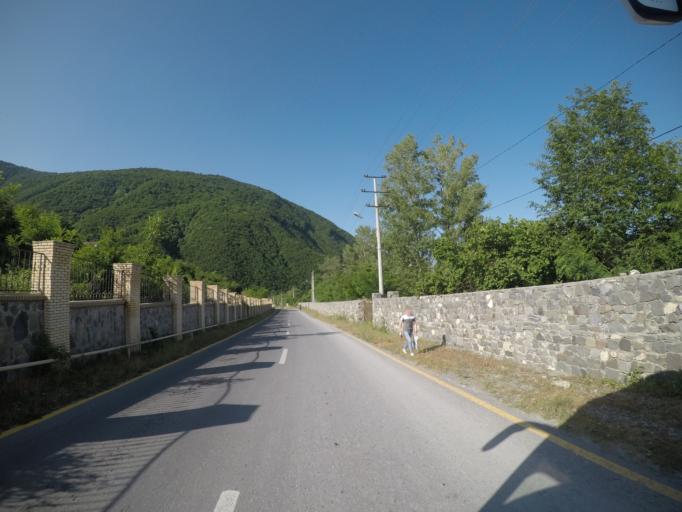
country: AZ
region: Shaki City
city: Sheki
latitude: 41.2478
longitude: 47.2018
